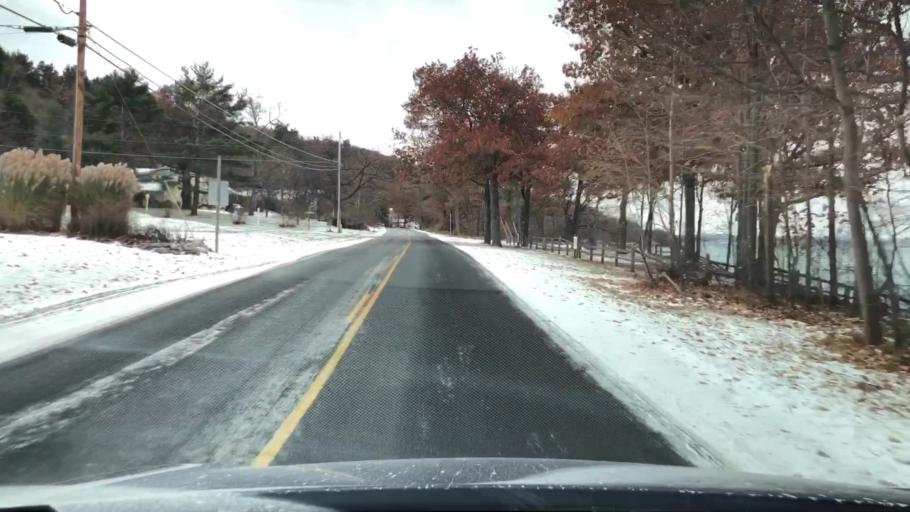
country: US
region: Michigan
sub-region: Grand Traverse County
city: Traverse City
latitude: 44.8055
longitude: -85.5813
